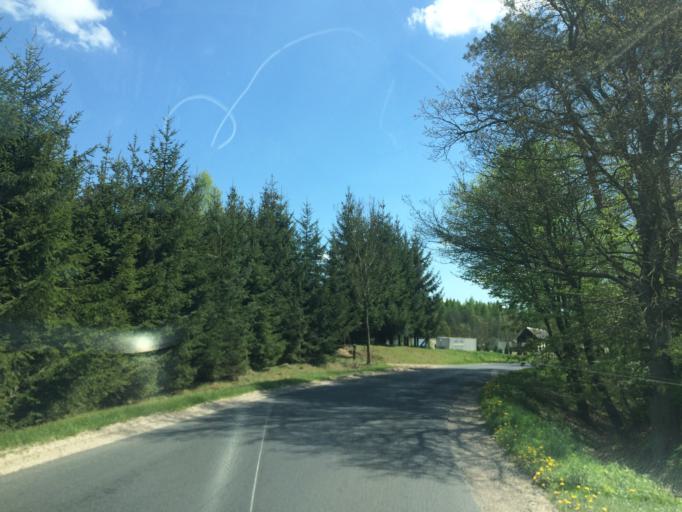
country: PL
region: Warmian-Masurian Voivodeship
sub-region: Powiat nowomiejski
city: Biskupiec
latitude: 53.3998
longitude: 19.3571
